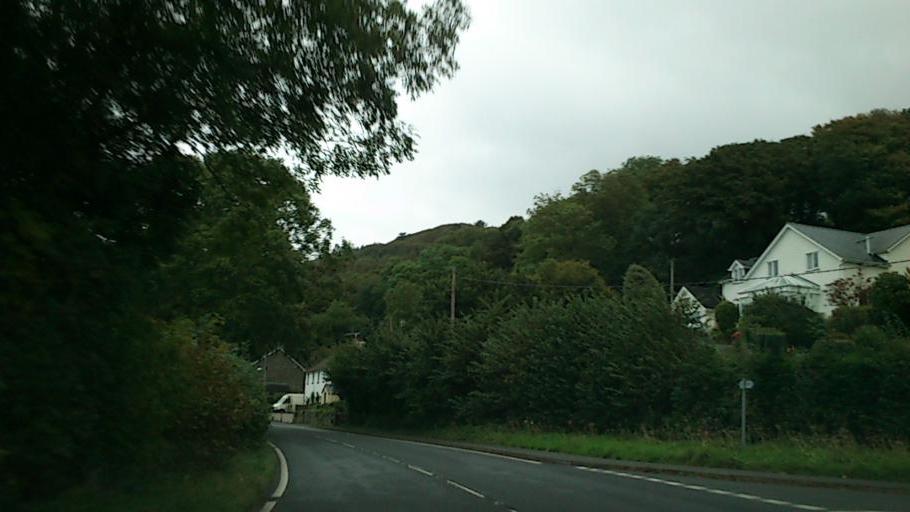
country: GB
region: Wales
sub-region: County of Ceredigion
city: Bow Street
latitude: 52.5130
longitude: -3.9755
